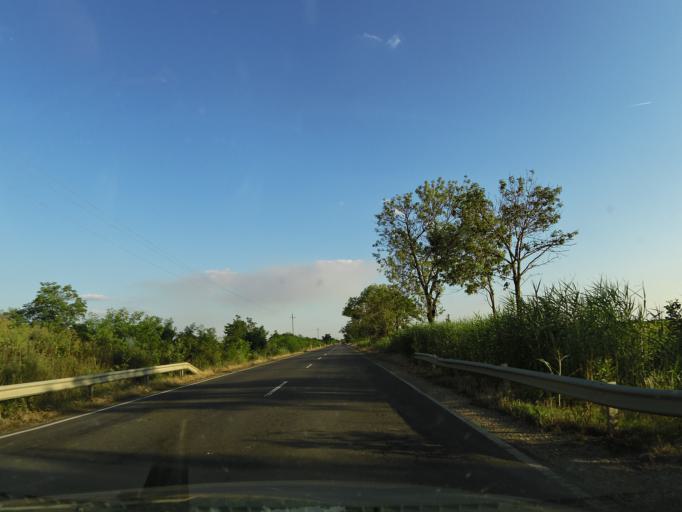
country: HU
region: Jasz-Nagykun-Szolnok
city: Kunszentmarton
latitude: 46.8690
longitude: 20.2654
